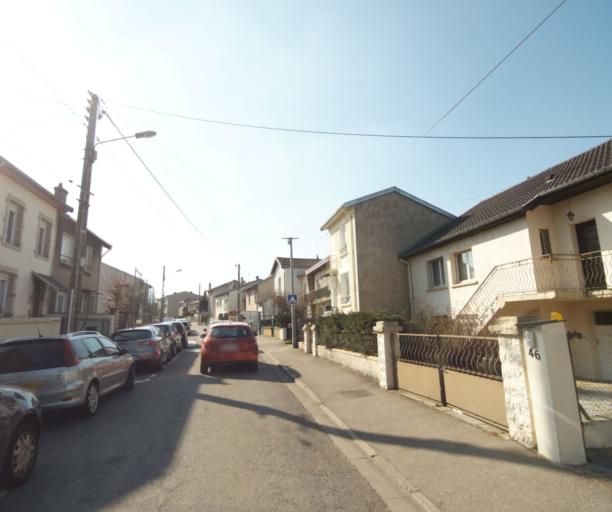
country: FR
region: Lorraine
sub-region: Departement de Meurthe-et-Moselle
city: Jarville-la-Malgrange
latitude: 48.6674
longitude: 6.2000
